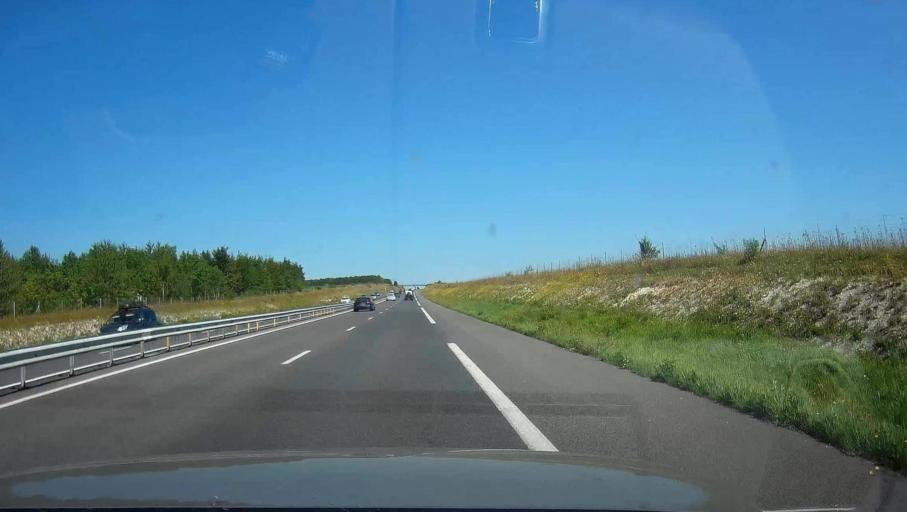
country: FR
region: Champagne-Ardenne
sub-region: Departement de l'Aube
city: Mailly-le-Camp
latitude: 48.7955
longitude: 4.2739
